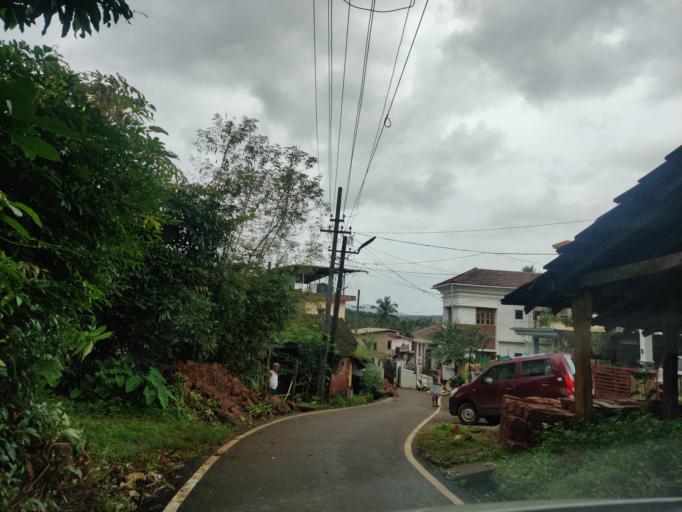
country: IN
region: Goa
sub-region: North Goa
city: Valpoy
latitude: 15.5268
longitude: 74.1418
